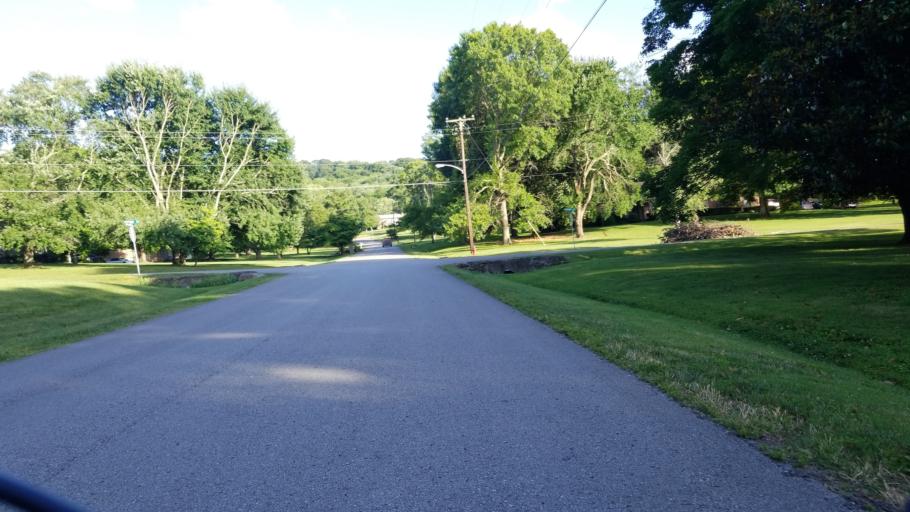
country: US
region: Tennessee
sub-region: Davidson County
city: Forest Hills
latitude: 36.0394
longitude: -86.8583
